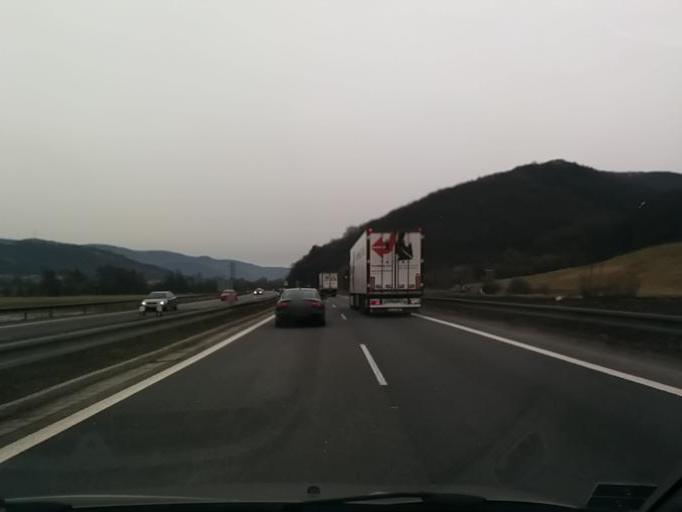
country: SK
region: Banskobystricky
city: Ziar nad Hronom
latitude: 48.5870
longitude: 18.9110
